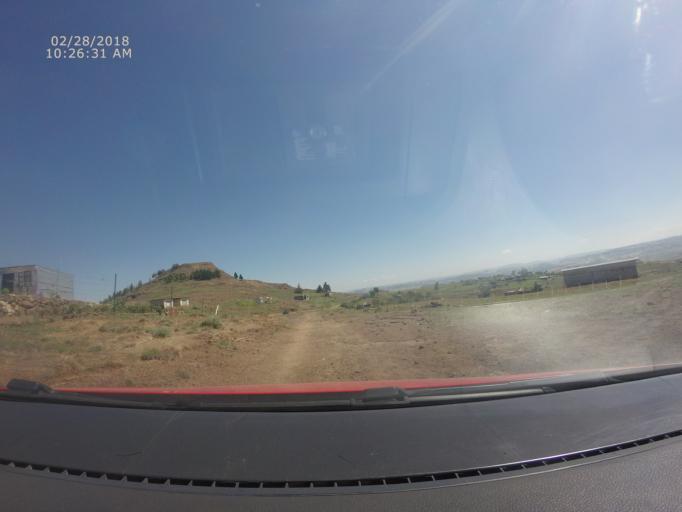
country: LS
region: Berea
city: Teyateyaneng
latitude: -29.2212
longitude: 27.8674
